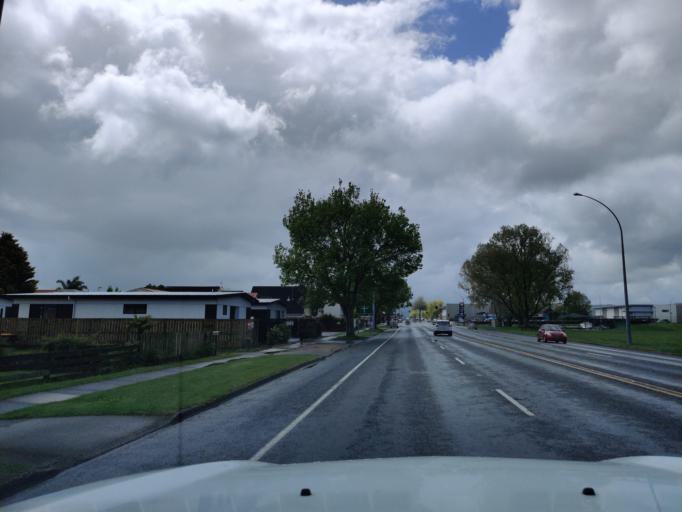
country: NZ
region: Bay of Plenty
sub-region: Rotorua District
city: Rotorua
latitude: -38.1398
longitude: 176.2446
